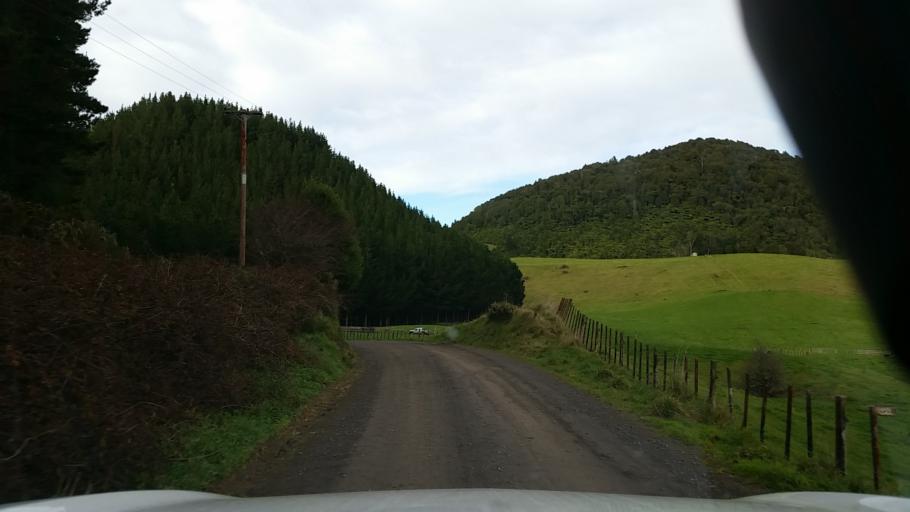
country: NZ
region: Bay of Plenty
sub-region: Rotorua District
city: Rotorua
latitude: -38.2182
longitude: 176.1590
